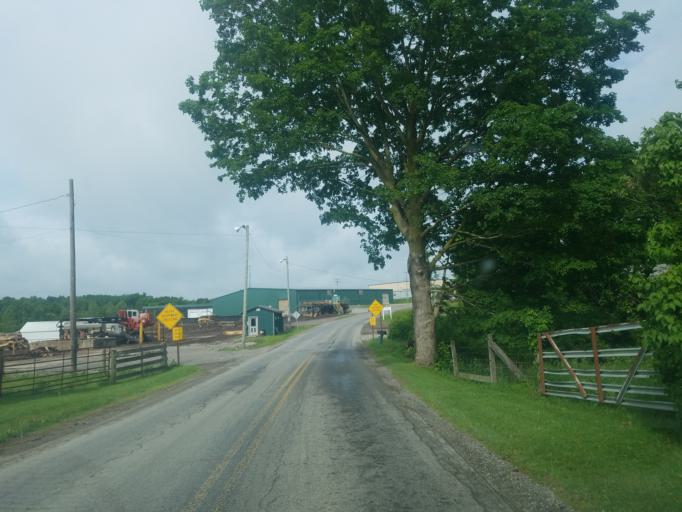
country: US
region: Ohio
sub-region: Holmes County
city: Millersburg
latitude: 40.5074
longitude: -81.8797
